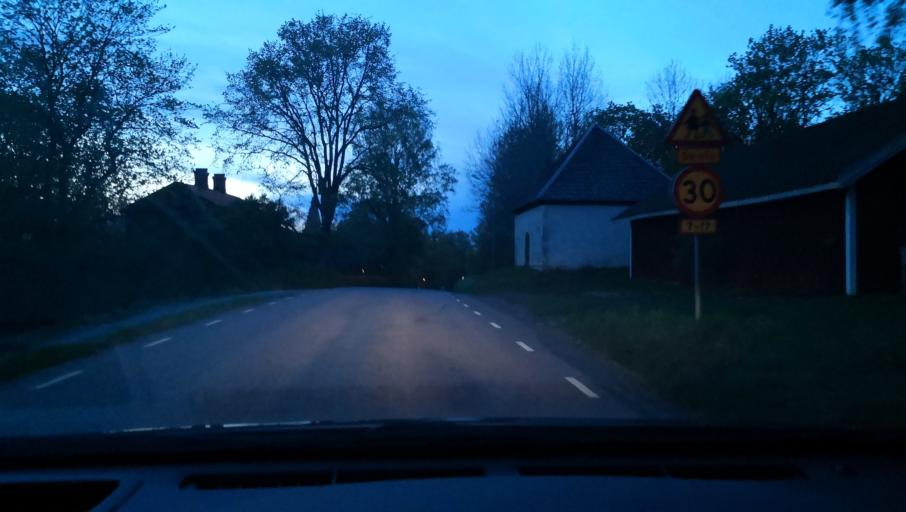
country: SE
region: OErebro
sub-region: Hallsbergs Kommun
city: Hallsberg
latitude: 59.1036
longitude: 15.0069
